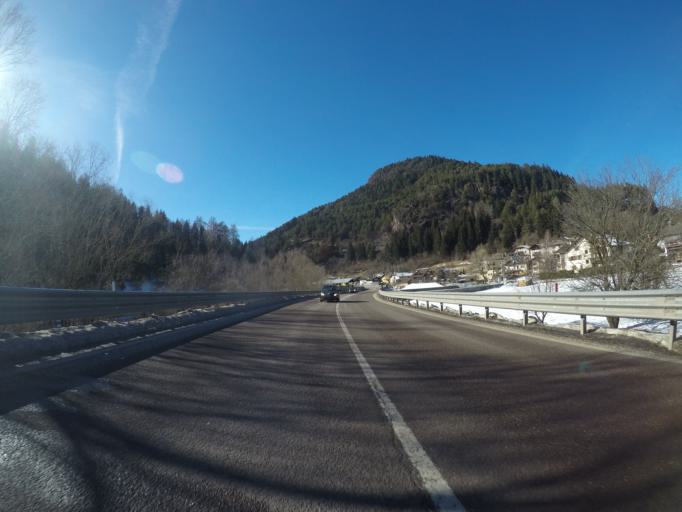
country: IT
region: Trentino-Alto Adige
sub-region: Provincia di Trento
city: Castello Molina di Fiemme
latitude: 46.2707
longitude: 11.4166
